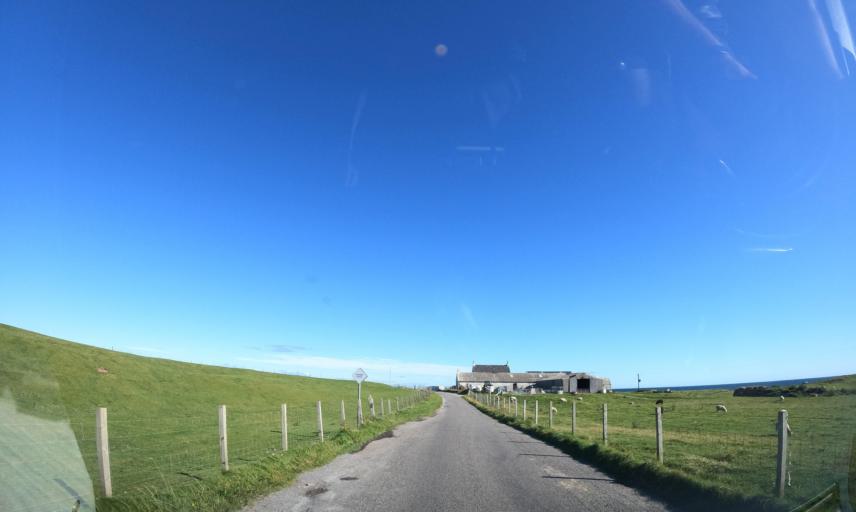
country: GB
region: Scotland
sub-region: Eilean Siar
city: Barra
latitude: 56.4822
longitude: -6.8867
